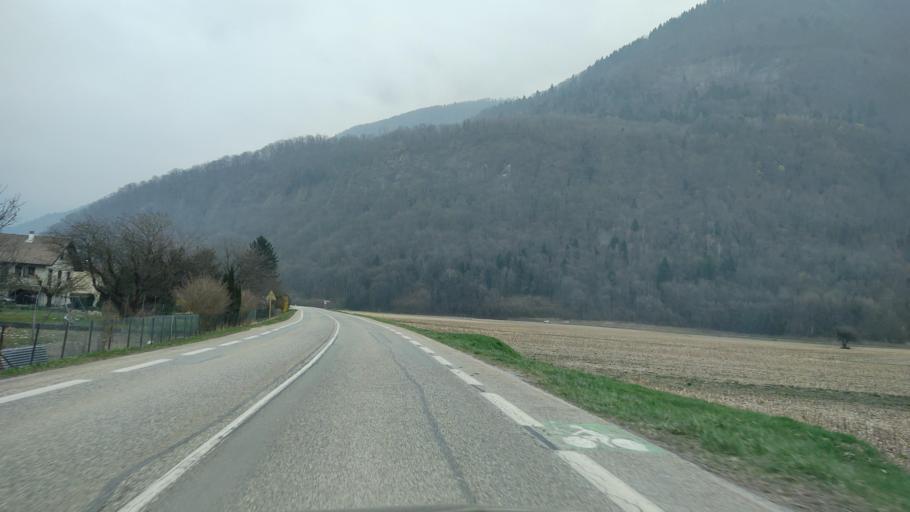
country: FR
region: Rhone-Alpes
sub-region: Departement de la Savoie
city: Aiton
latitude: 45.5497
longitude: 6.2356
